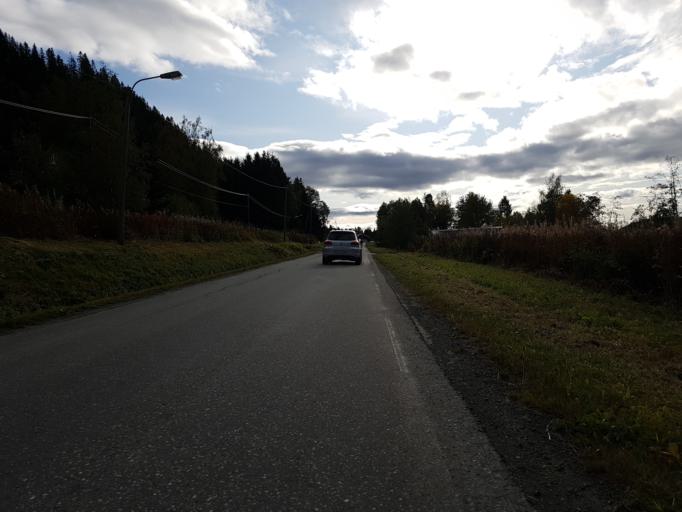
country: NO
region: Sor-Trondelag
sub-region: Klaebu
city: Klaebu
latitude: 63.3967
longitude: 10.5552
